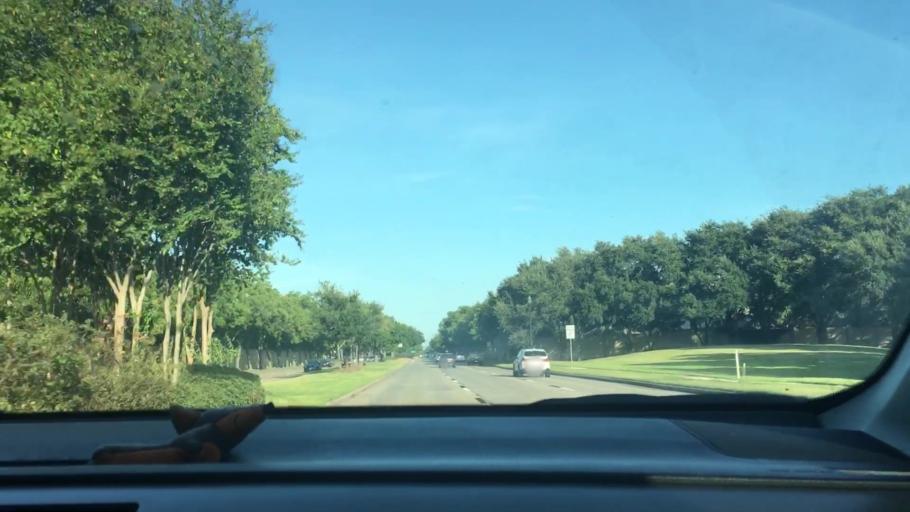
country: US
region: Texas
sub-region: Fort Bend County
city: Sugar Land
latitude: 29.5940
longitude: -95.6105
